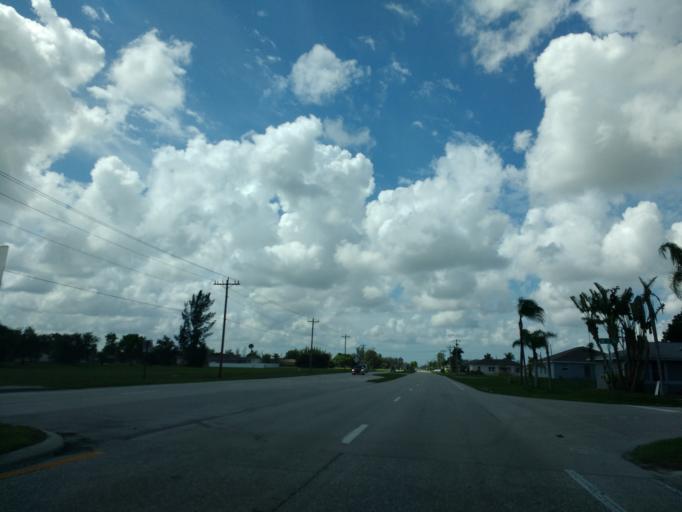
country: US
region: Florida
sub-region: Lee County
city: Cape Coral
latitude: 26.6300
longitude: -82.0072
